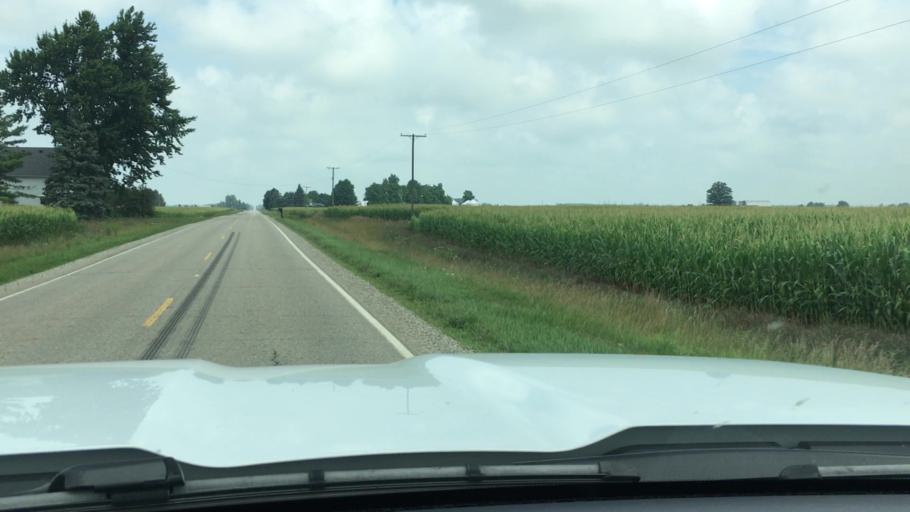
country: US
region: Michigan
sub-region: Sanilac County
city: Marlette
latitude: 43.3807
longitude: -83.0066
